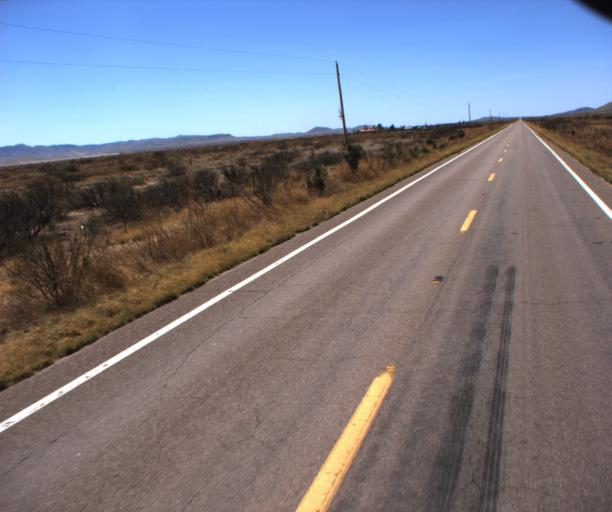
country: US
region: Arizona
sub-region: Cochise County
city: Douglas
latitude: 31.7334
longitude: -109.1031
